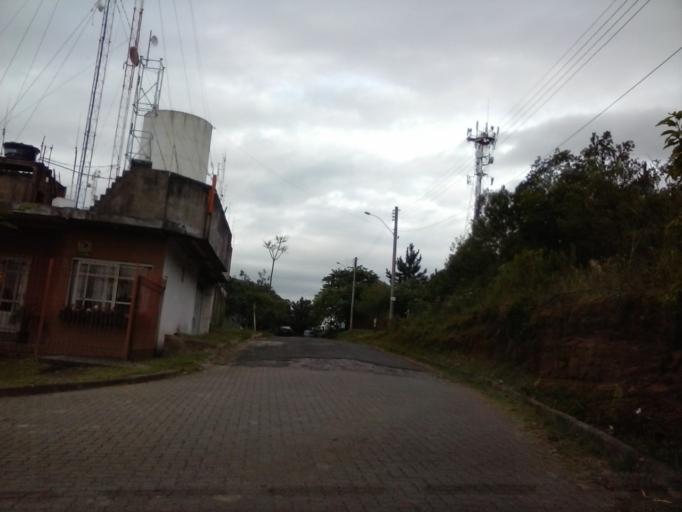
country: BR
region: Rio Grande do Sul
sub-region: Sapucaia Do Sul
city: Sapucaia
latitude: -29.8462
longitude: -51.1095
